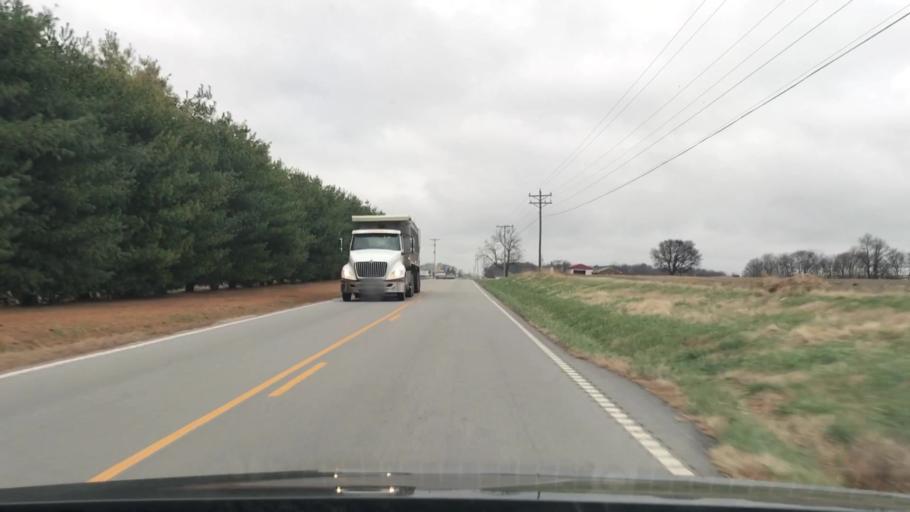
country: US
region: Kentucky
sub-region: Todd County
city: Guthrie
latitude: 36.6729
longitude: -87.1982
